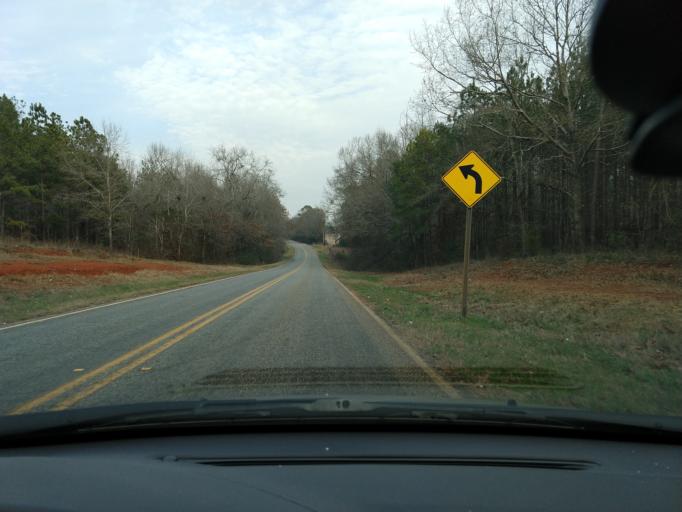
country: US
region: Georgia
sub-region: Webster County
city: Preston
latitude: 32.0135
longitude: -84.4107
